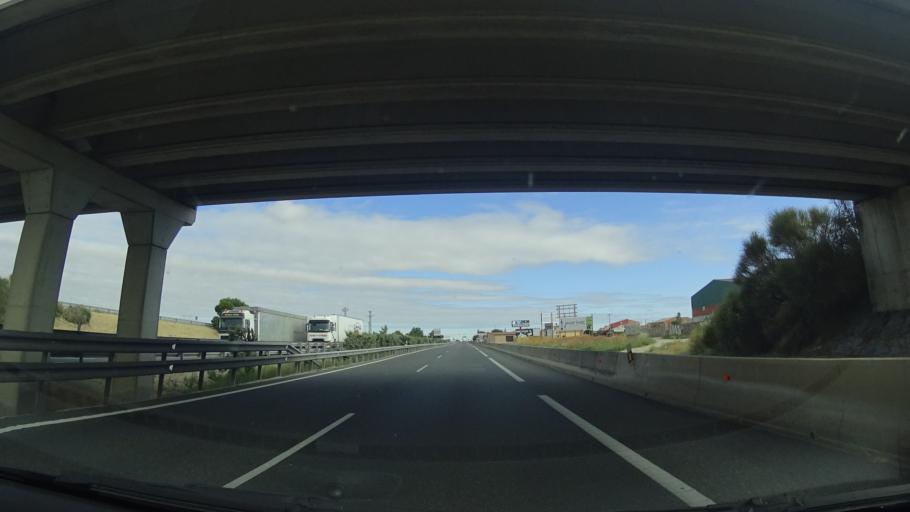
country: ES
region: Castille and Leon
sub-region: Provincia de Valladolid
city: Ataquines
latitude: 41.1772
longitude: -4.8054
